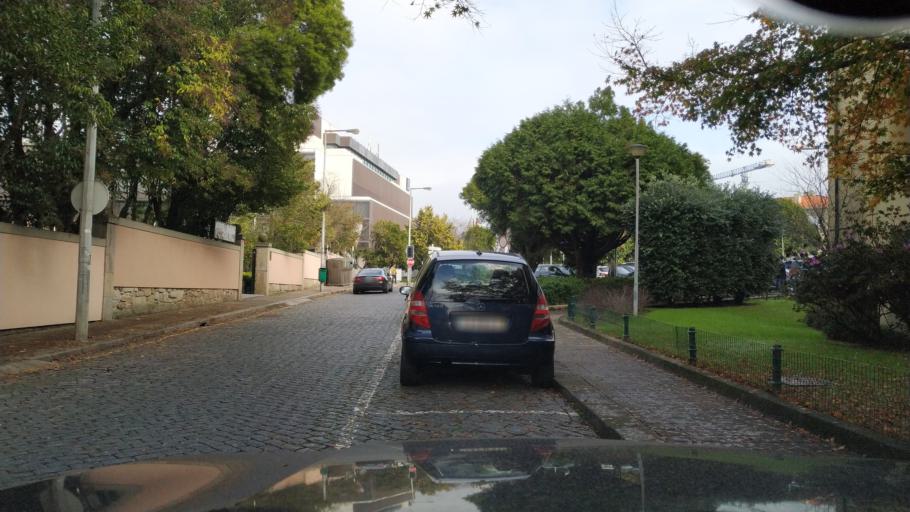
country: PT
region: Porto
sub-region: Matosinhos
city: Senhora da Hora
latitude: 41.1623
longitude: -8.6395
